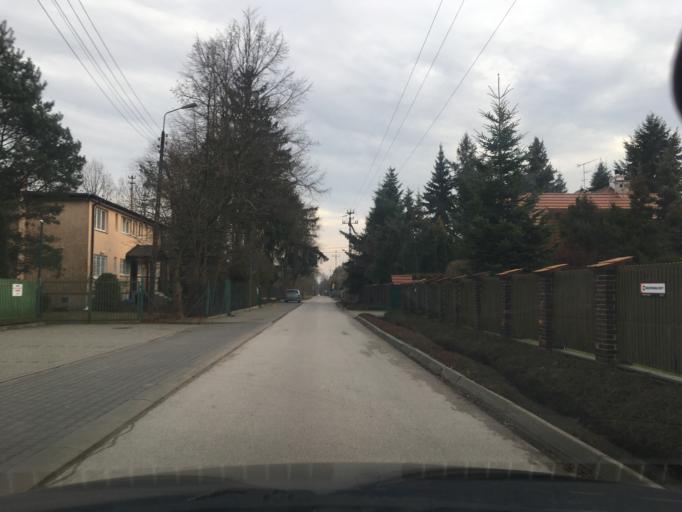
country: PL
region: Masovian Voivodeship
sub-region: Powiat piaseczynski
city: Lesznowola
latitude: 52.0382
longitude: 20.9549
